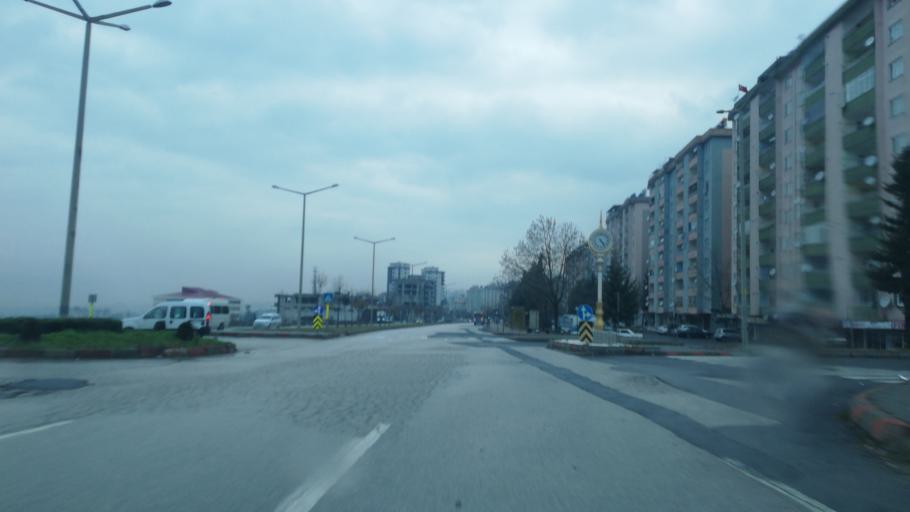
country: TR
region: Kahramanmaras
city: Kahramanmaras
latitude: 37.5824
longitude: 36.9867
